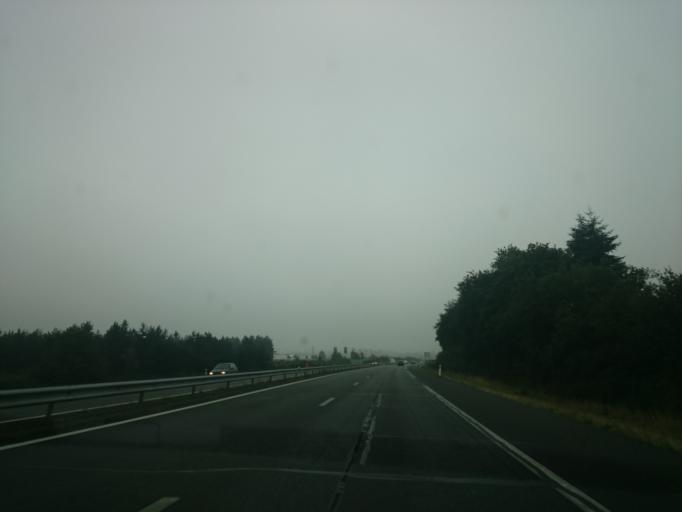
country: FR
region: Brittany
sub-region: Departement d'Ille-et-Vilaine
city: Bain-de-Bretagne
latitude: 47.8644
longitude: -1.6911
